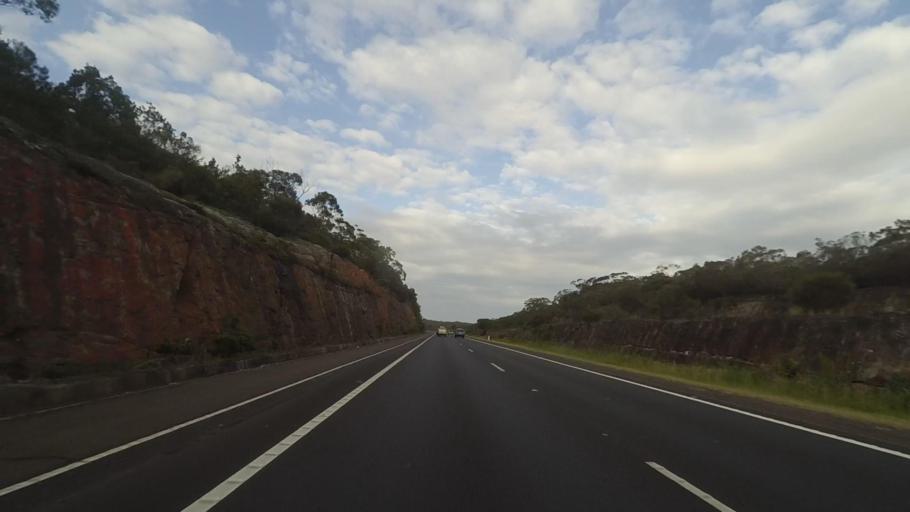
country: AU
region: New South Wales
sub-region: Wollongong
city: Bulli
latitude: -34.2923
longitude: 150.9215
